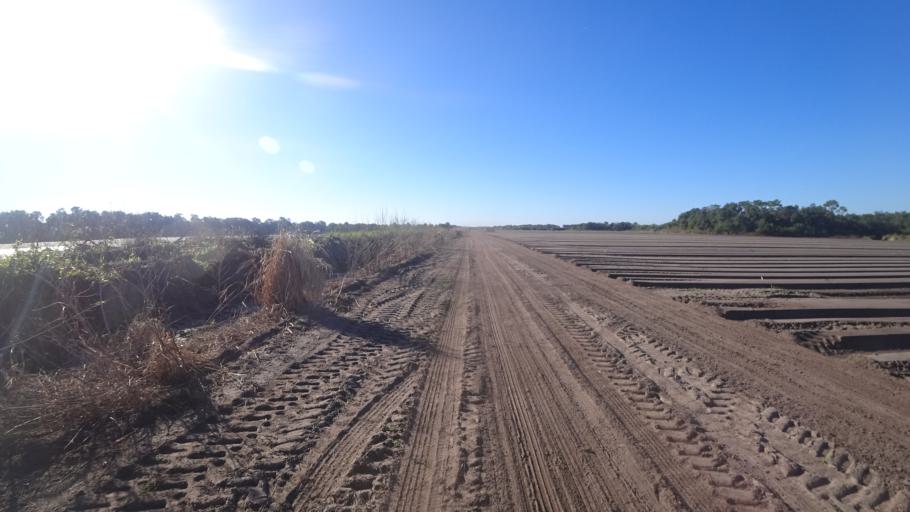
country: US
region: Florida
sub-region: Hillsborough County
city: Ruskin
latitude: 27.6432
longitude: -82.4358
